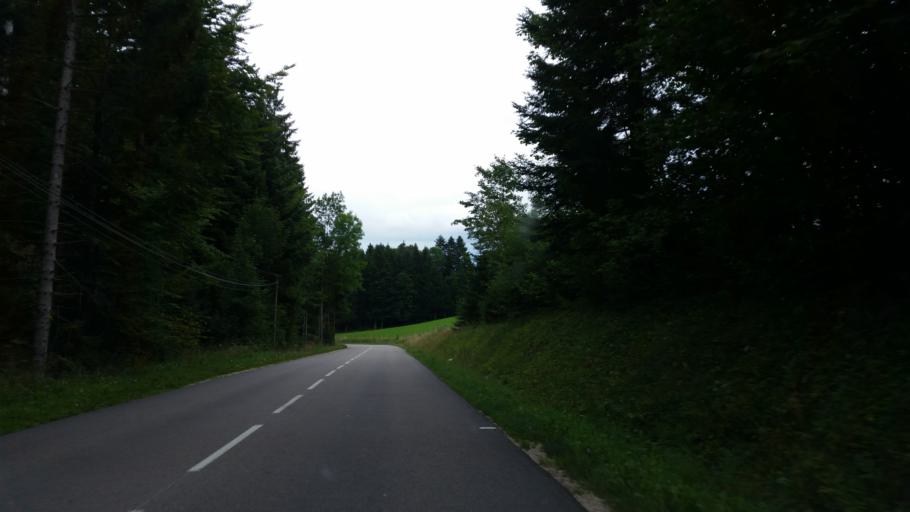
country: FR
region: Franche-Comte
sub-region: Departement du Doubs
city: Charquemont
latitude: 47.1738
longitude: 6.8215
